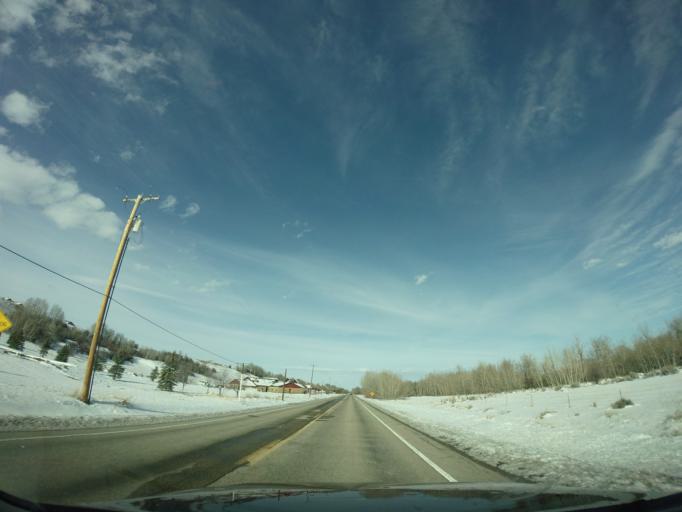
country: US
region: Montana
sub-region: Carbon County
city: Red Lodge
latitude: 45.2095
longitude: -109.2436
